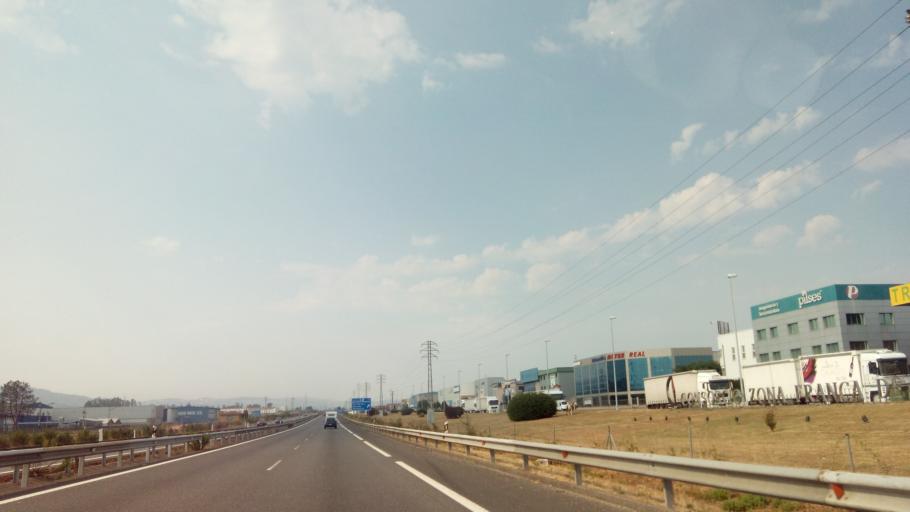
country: ES
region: Galicia
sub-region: Provincia de Pontevedra
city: Porrino
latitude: 42.1224
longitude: -8.6221
